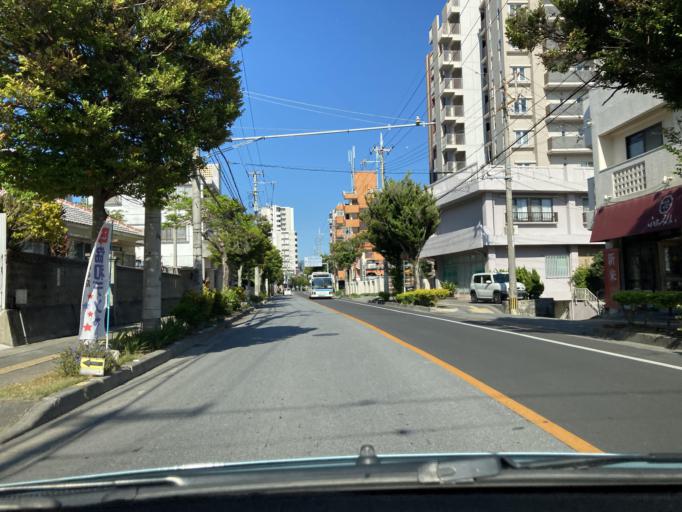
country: JP
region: Okinawa
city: Naha-shi
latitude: 26.2292
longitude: 127.7214
